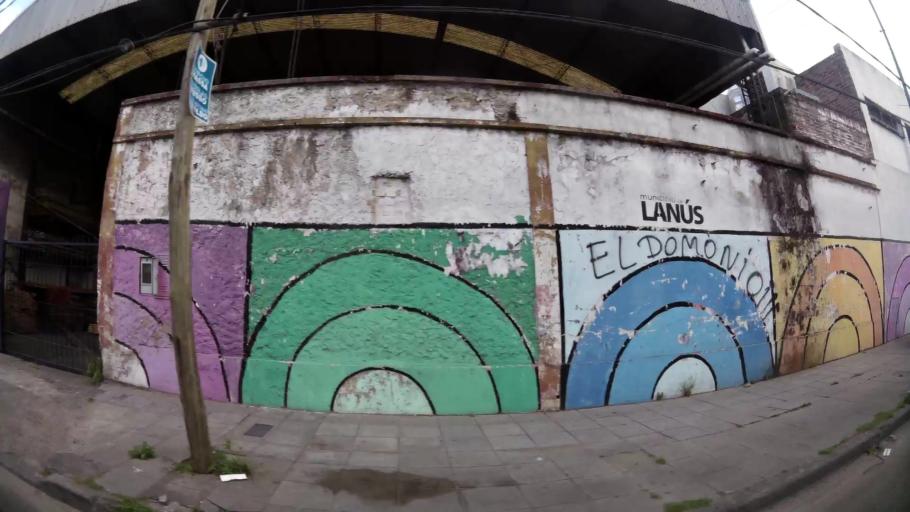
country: AR
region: Buenos Aires
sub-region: Partido de Lanus
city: Lanus
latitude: -34.7012
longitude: -58.3652
